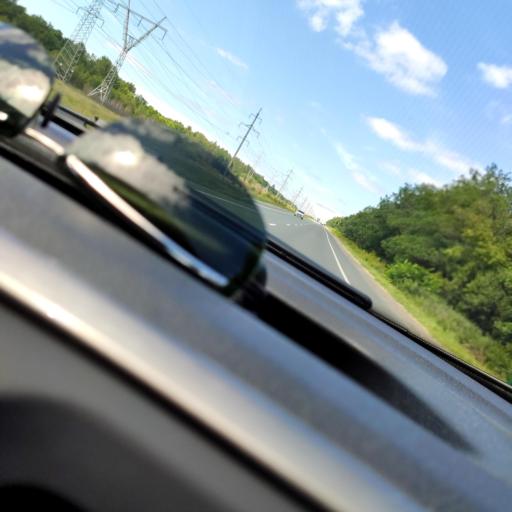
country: RU
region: Samara
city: Bogatyr'
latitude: 53.4961
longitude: 49.9623
